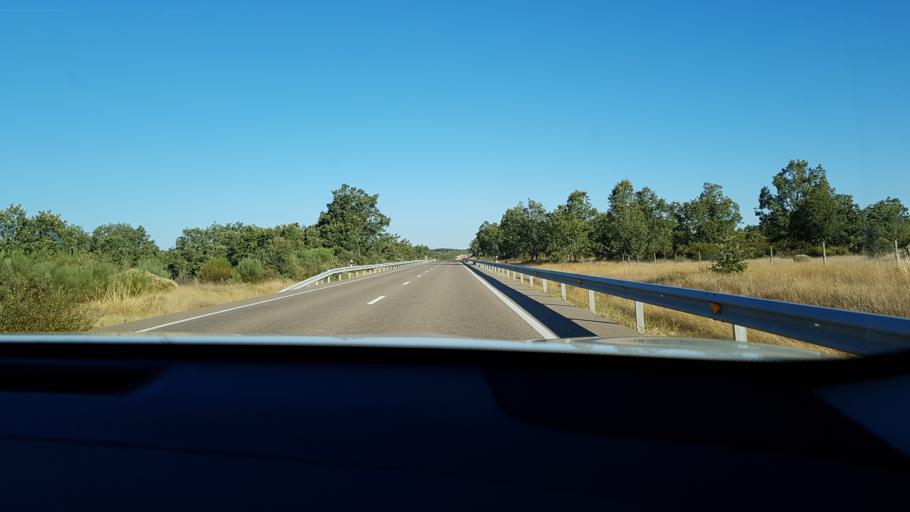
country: ES
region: Castille and Leon
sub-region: Provincia de Zamora
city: Samir de los Canos
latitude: 41.6622
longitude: -6.2070
